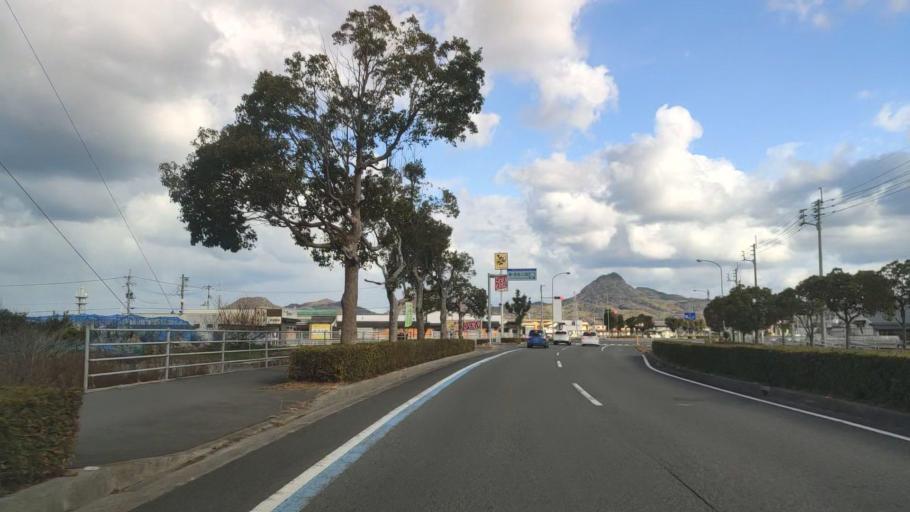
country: JP
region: Ehime
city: Hojo
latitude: 33.9664
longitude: 132.7792
